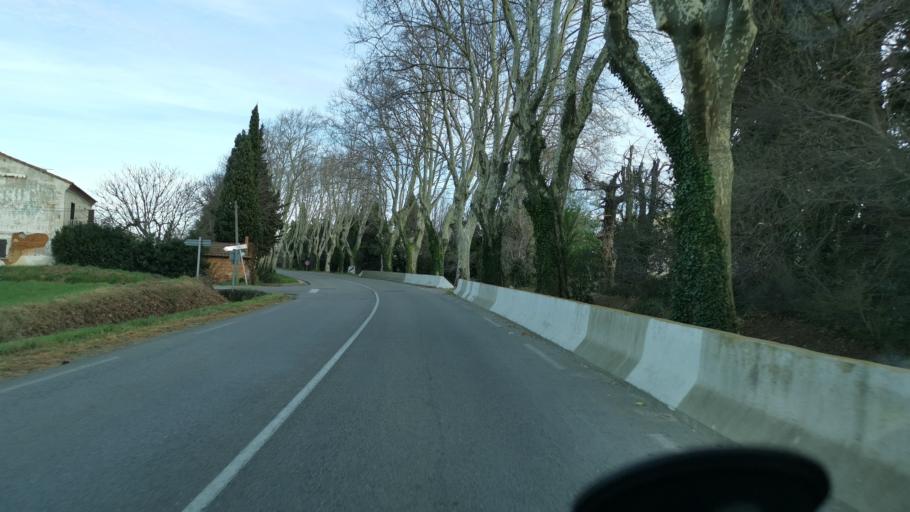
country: FR
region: Provence-Alpes-Cote d'Azur
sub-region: Departement des Bouches-du-Rhone
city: Saint-Martin-de-Crau
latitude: 43.6363
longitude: 4.7481
